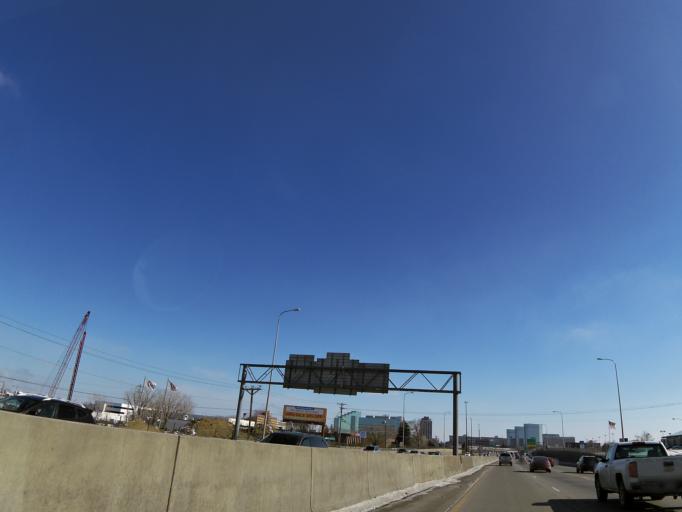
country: US
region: Minnesota
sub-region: Hennepin County
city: Edina
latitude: 44.8586
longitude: -93.3460
